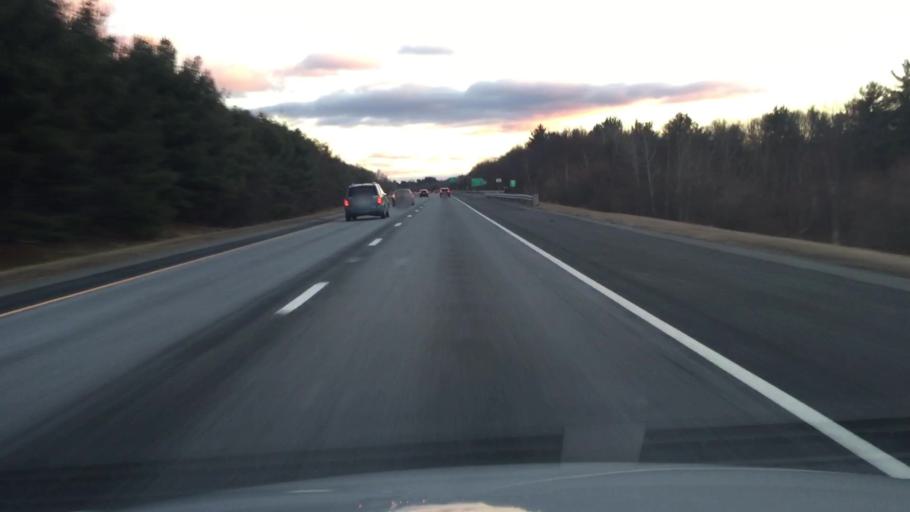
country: US
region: Massachusetts
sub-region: Worcester County
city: West Boylston
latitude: 42.3586
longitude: -71.8125
